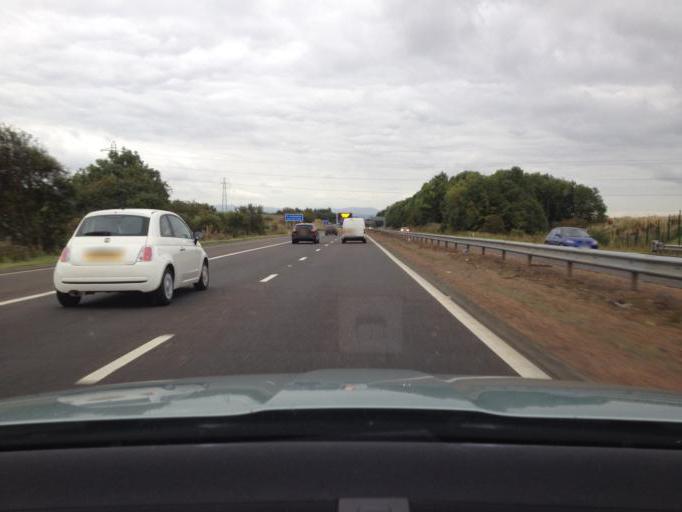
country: GB
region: Scotland
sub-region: Fife
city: Crossgates
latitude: 56.0623
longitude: -3.3872
